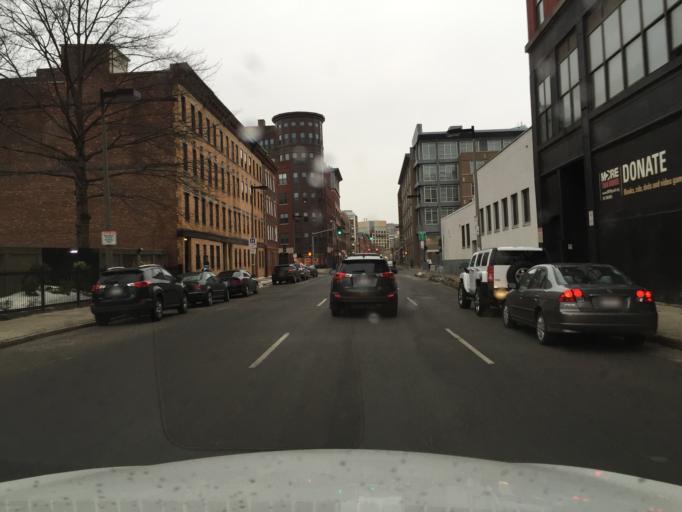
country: US
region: Massachusetts
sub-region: Suffolk County
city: Boston
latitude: 42.3432
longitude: -71.0633
